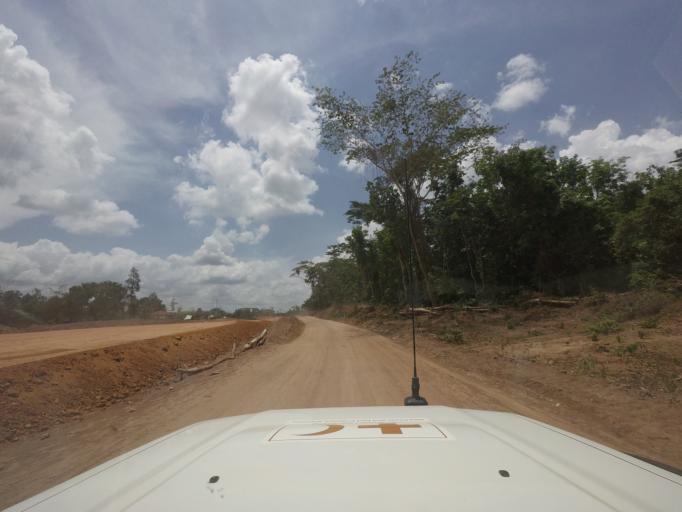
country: LR
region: Nimba
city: Sanniquellie
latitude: 7.2409
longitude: -8.8765
